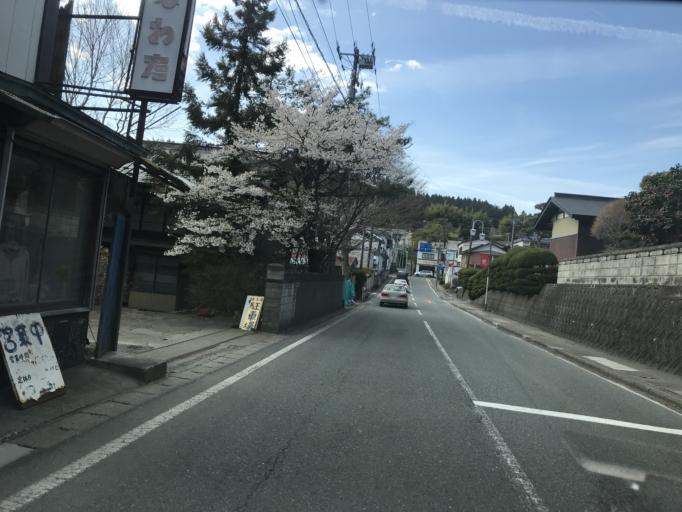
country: JP
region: Iwate
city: Ichinoseki
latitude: 38.8620
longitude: 141.3504
